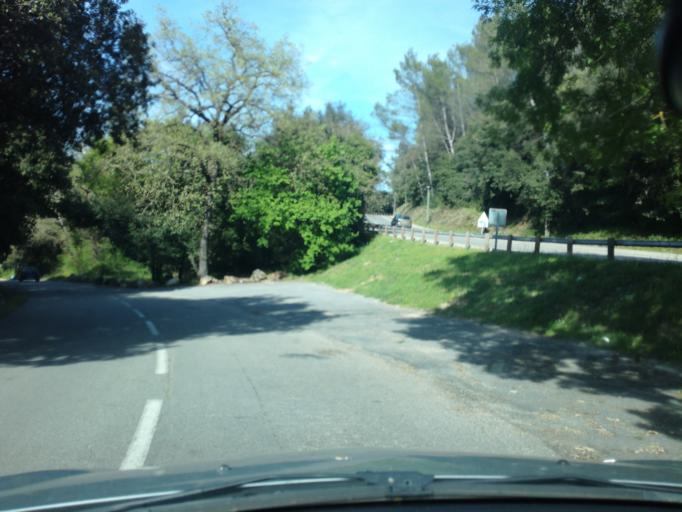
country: FR
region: Provence-Alpes-Cote d'Azur
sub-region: Departement des Alpes-Maritimes
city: La Roquette-sur-Siagne
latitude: 43.6158
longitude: 6.9513
